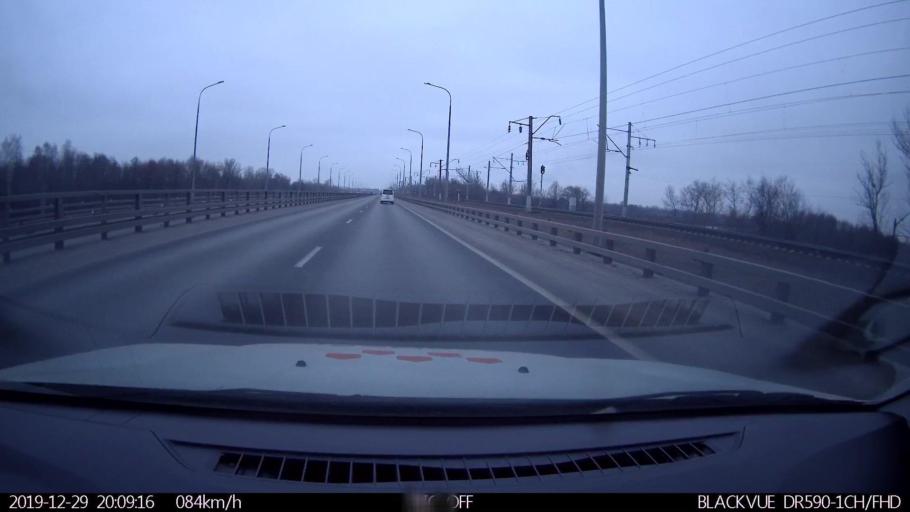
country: RU
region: Nizjnij Novgorod
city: Neklyudovo
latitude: 56.3773
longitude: 43.9539
